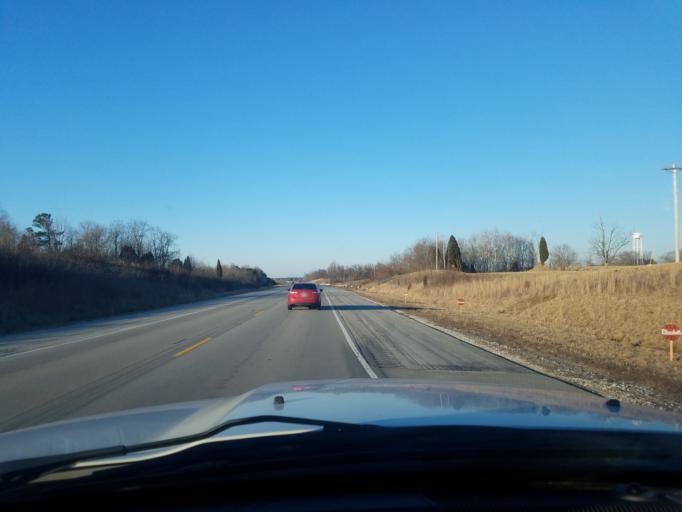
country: US
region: Indiana
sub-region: Perry County
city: Tell City
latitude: 38.1274
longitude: -86.6056
